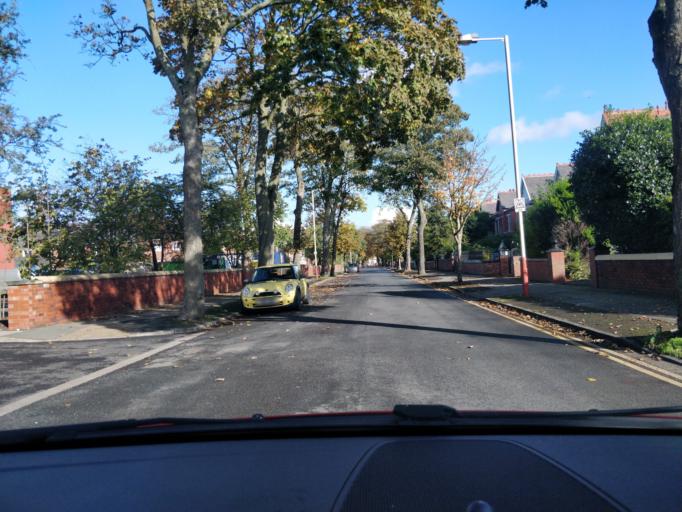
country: GB
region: England
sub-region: Sefton
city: Southport
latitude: 53.6381
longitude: -2.9857
